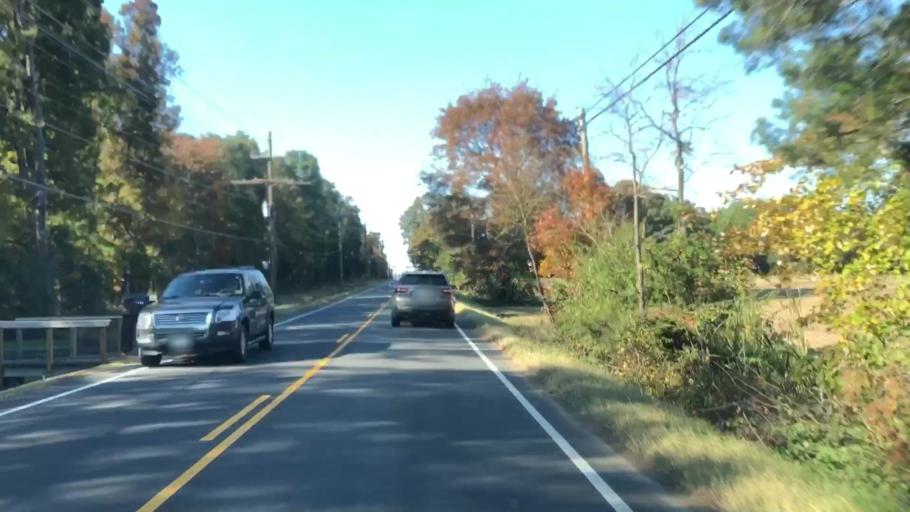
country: US
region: Virginia
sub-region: Prince William County
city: Linton Hall
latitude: 38.7460
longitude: -77.6086
